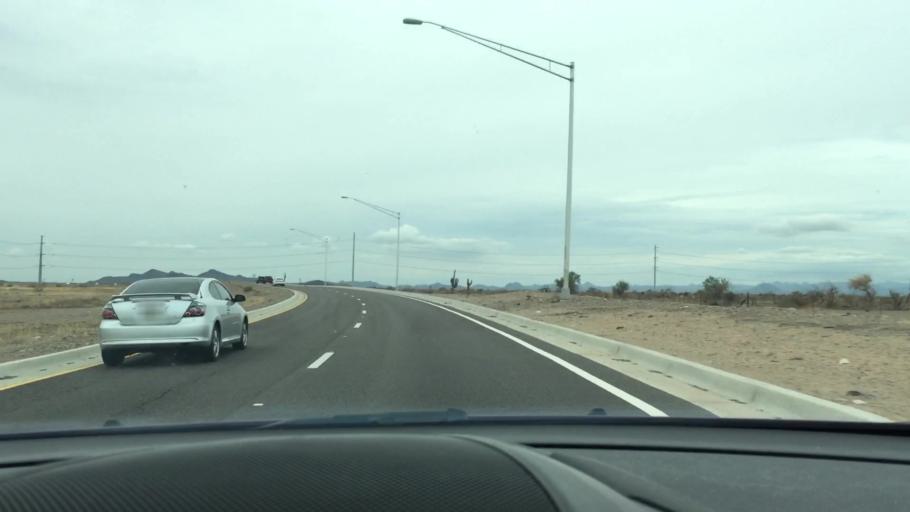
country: US
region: Arizona
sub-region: Maricopa County
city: Anthem
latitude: 33.7698
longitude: -112.1343
